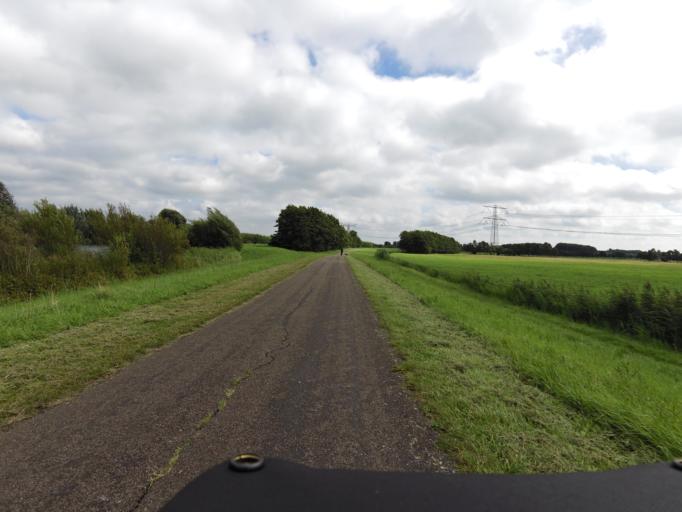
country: NL
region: South Holland
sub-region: Gemeente Spijkenisse
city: Spijkenisse
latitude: 51.8439
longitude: 4.2571
